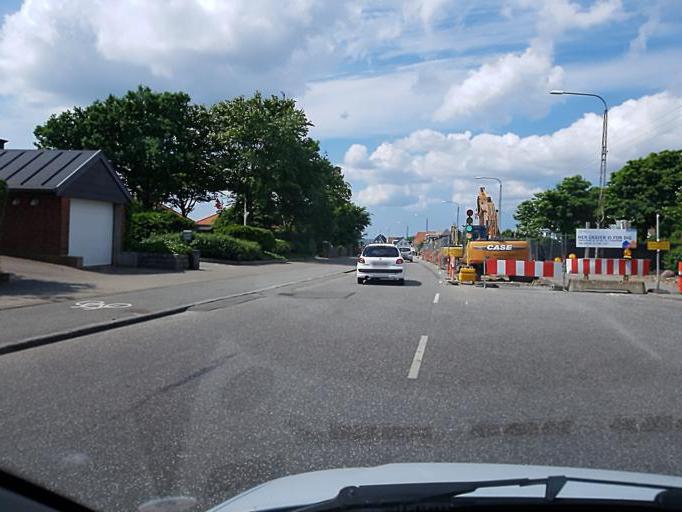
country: DK
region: South Denmark
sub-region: Fano Kommune
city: Nordby
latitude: 55.5200
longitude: 8.3610
